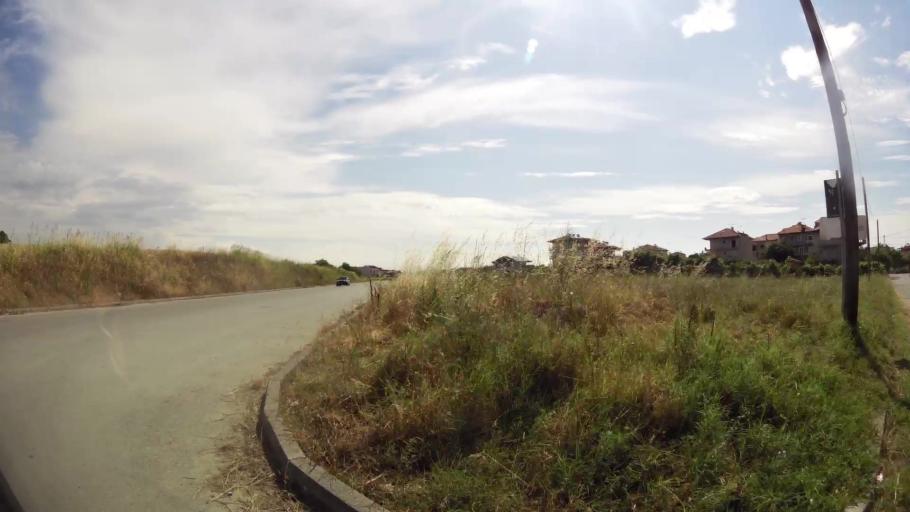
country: GR
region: Central Macedonia
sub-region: Nomos Pierias
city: Svoronos
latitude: 40.2766
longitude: 22.4828
